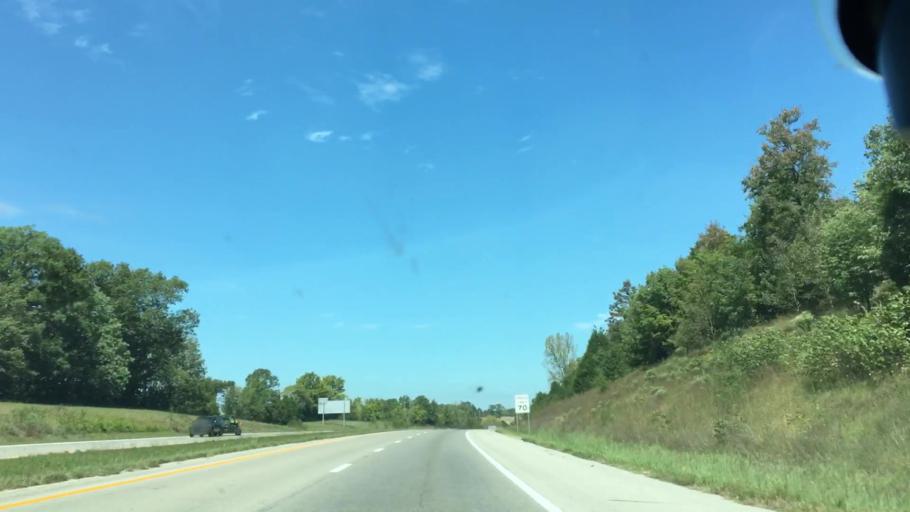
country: US
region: Kentucky
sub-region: Christian County
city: Hopkinsville
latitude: 36.9063
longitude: -87.4731
